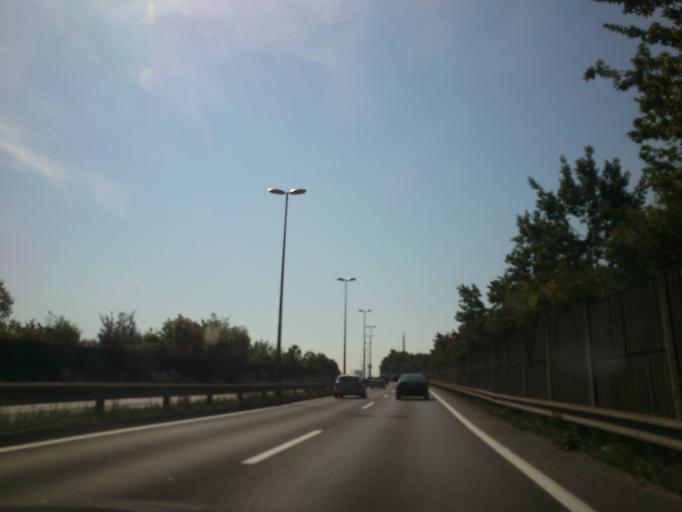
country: AT
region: Upper Austria
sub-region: Linz Stadt
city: Linz
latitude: 48.3147
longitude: 14.3064
